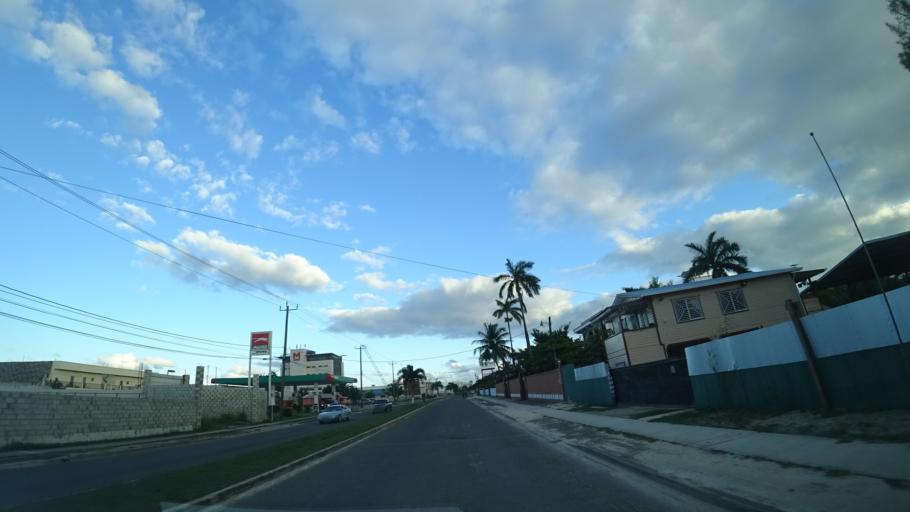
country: BZ
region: Belize
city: Belize City
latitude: 17.5087
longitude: -88.2067
